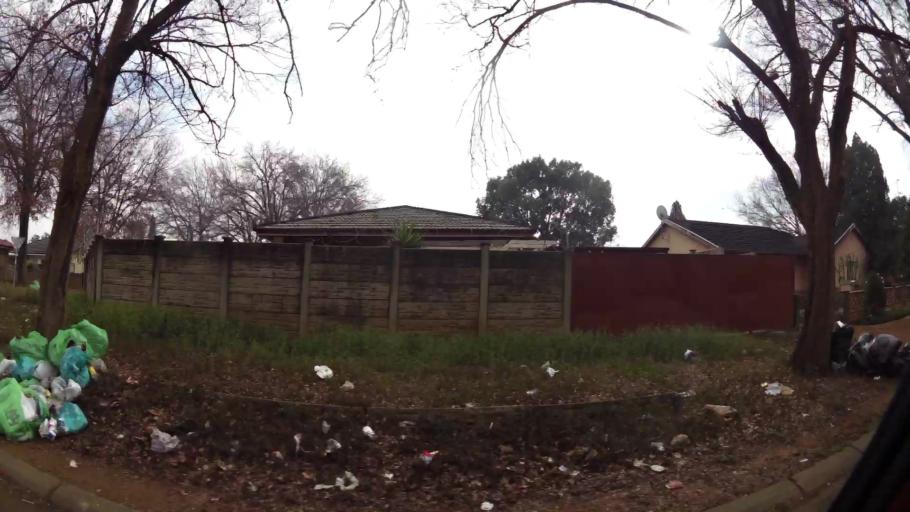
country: ZA
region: Gauteng
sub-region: Sedibeng District Municipality
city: Vanderbijlpark
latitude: -26.6996
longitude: 27.8416
